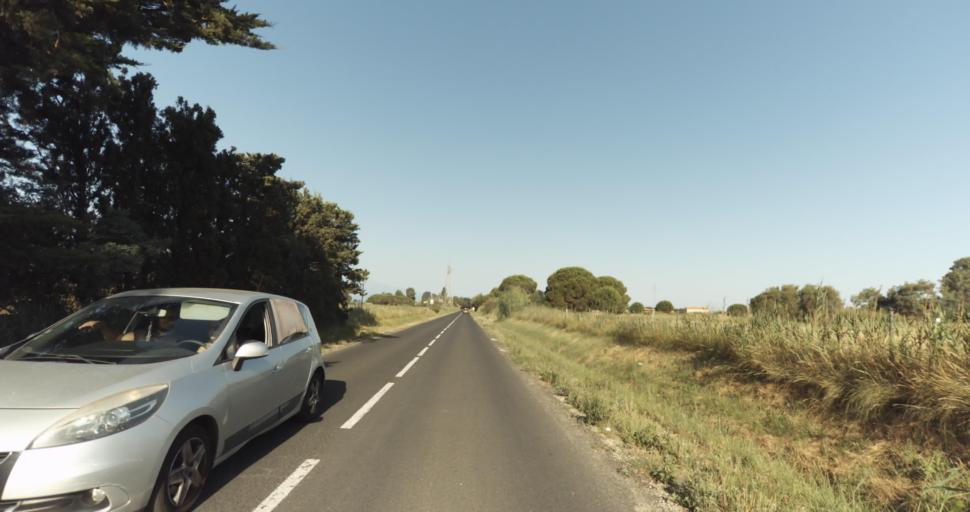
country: FR
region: Languedoc-Roussillon
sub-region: Departement des Pyrenees-Orientales
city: Alenya
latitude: 42.6365
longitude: 3.0033
